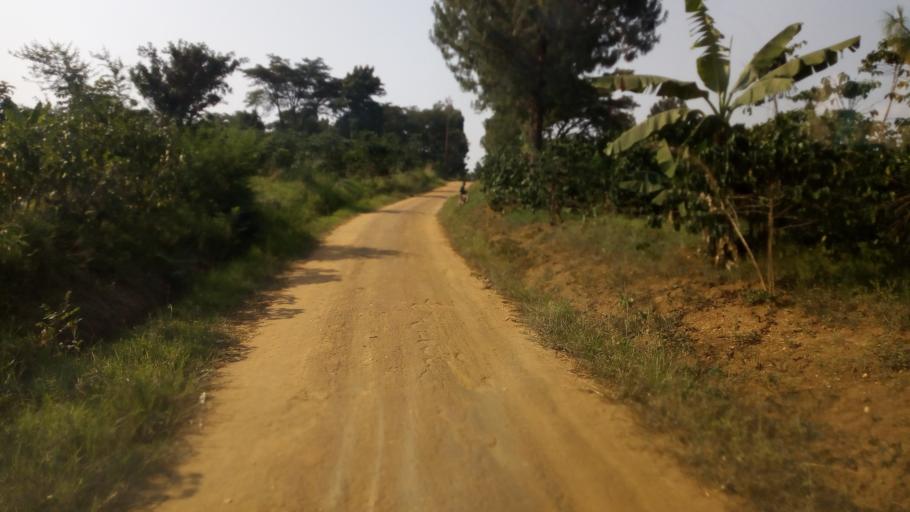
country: UG
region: Western Region
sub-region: Kanungu District
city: Ntungamo
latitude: -0.7668
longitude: 29.6565
